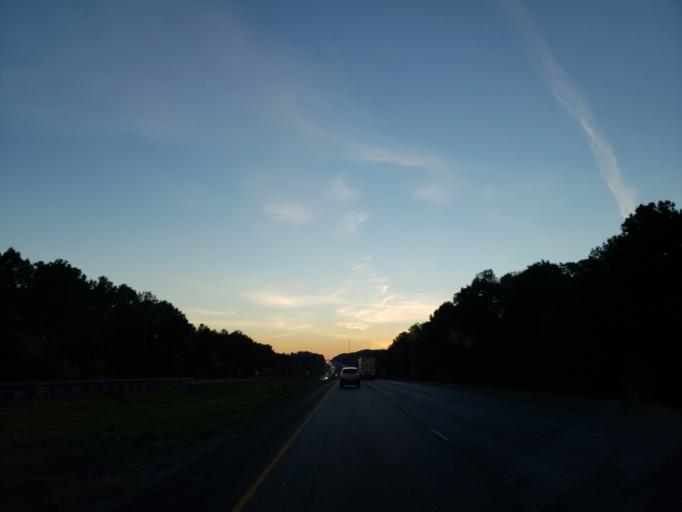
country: US
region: Alabama
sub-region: Sumter County
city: York
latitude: 32.5198
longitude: -88.3037
